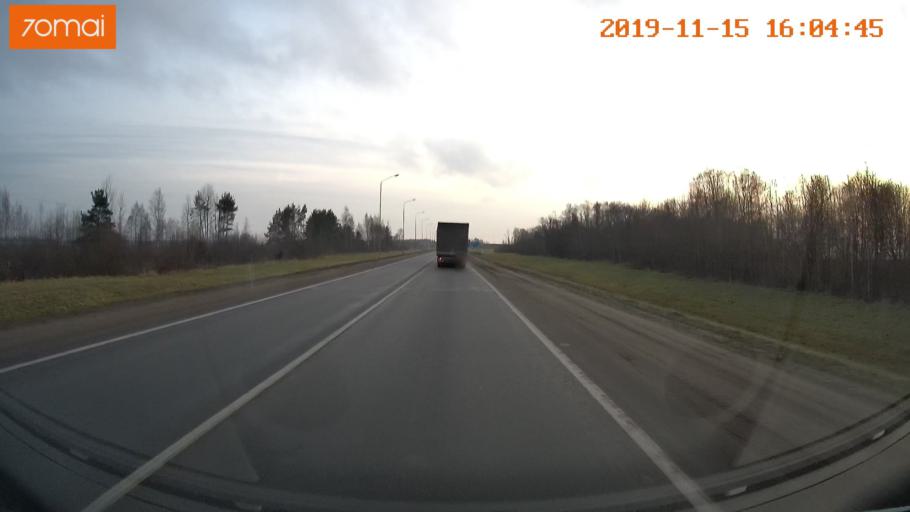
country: RU
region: Jaroslavl
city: Yaroslavl
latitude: 57.7444
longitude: 39.8984
